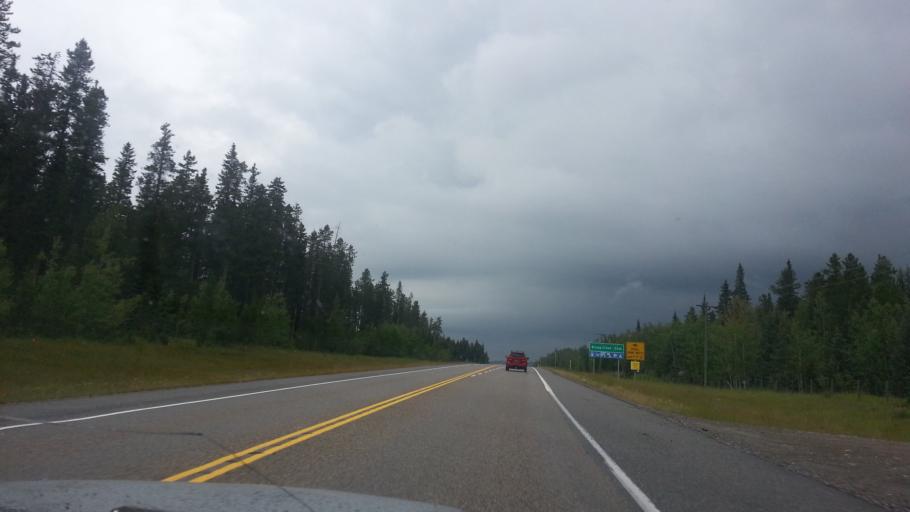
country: CA
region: Alberta
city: Cochrane
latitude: 50.9326
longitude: -114.5601
